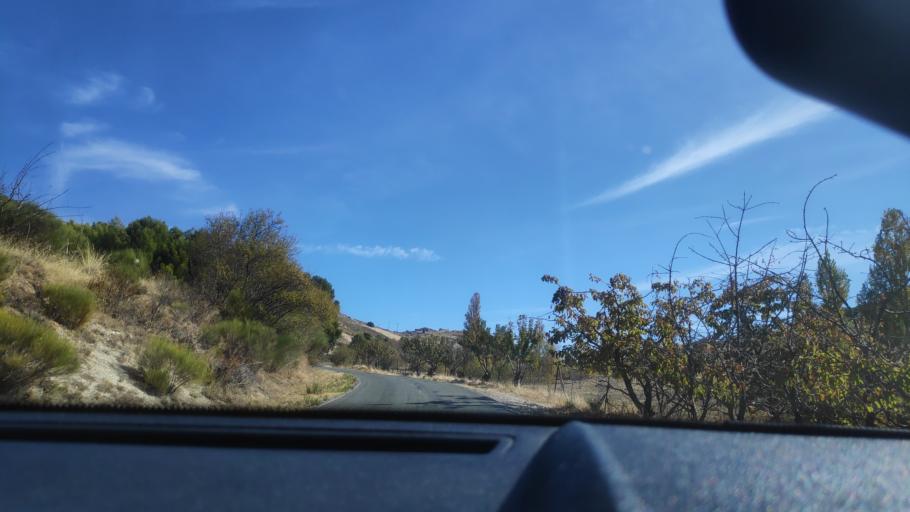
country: ES
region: Andalusia
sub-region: Provincia de Jaen
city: Torres
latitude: 37.7864
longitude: -3.4890
